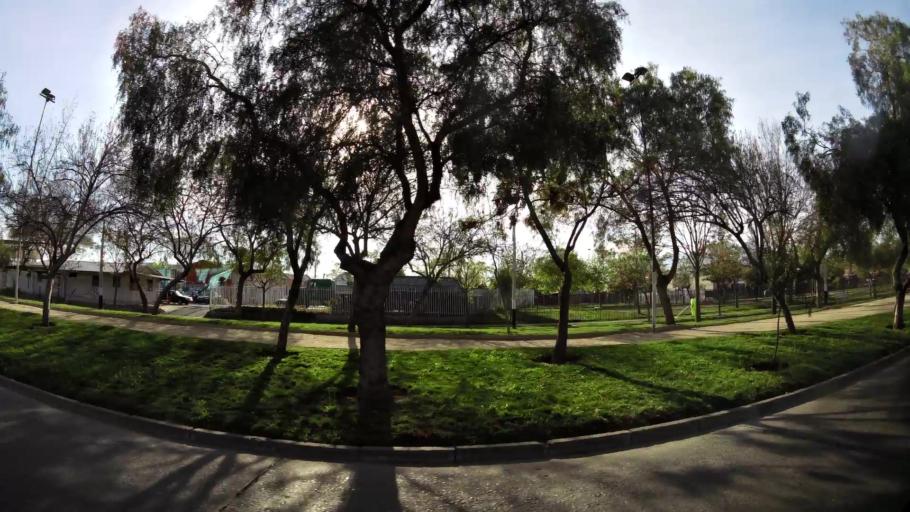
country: CL
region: Santiago Metropolitan
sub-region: Provincia de Cordillera
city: Puente Alto
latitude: -33.6108
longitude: -70.5918
